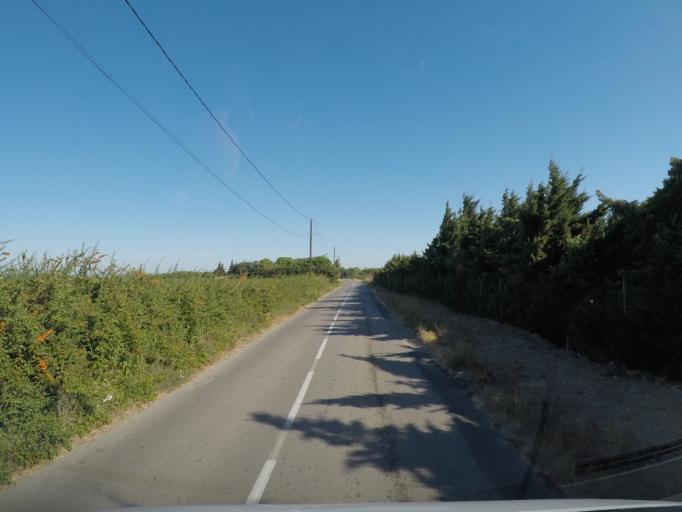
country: FR
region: Languedoc-Roussillon
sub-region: Departement de l'Aude
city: Narbonne
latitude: 43.1505
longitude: 3.0080
